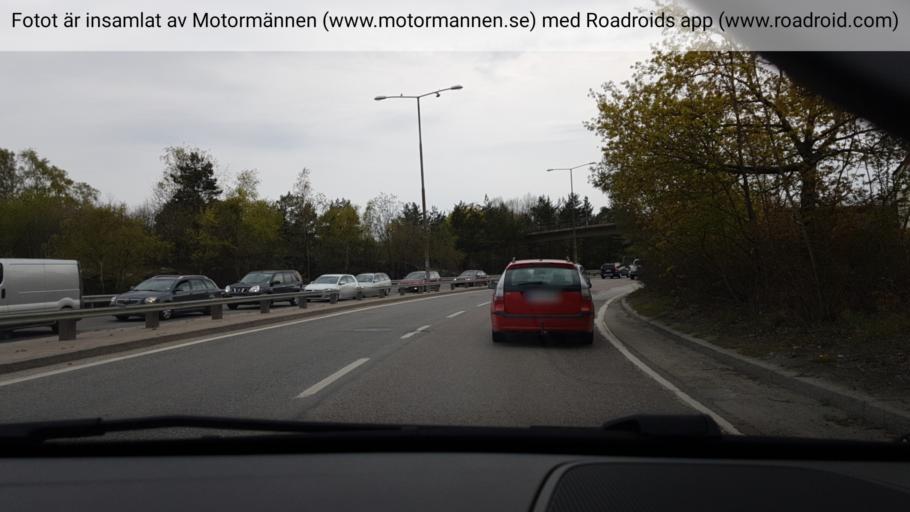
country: SE
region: Stockholm
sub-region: Stockholms Kommun
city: Arsta
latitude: 59.2925
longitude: 18.0330
